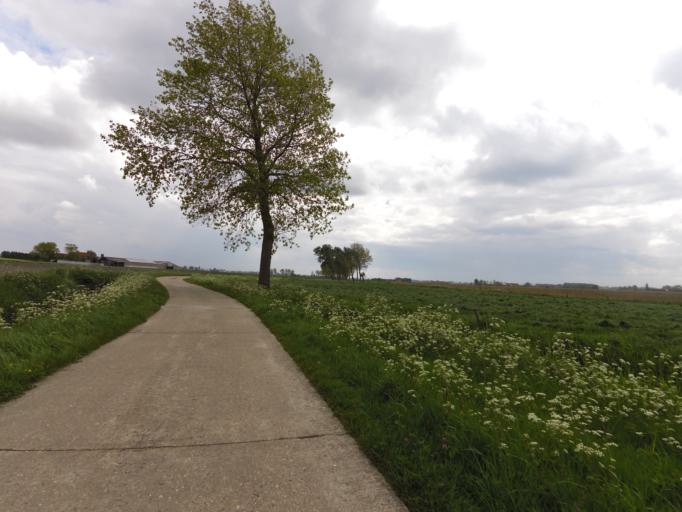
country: BE
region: Flanders
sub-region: Provincie West-Vlaanderen
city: Middelkerke
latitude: 51.1184
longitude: 2.8487
